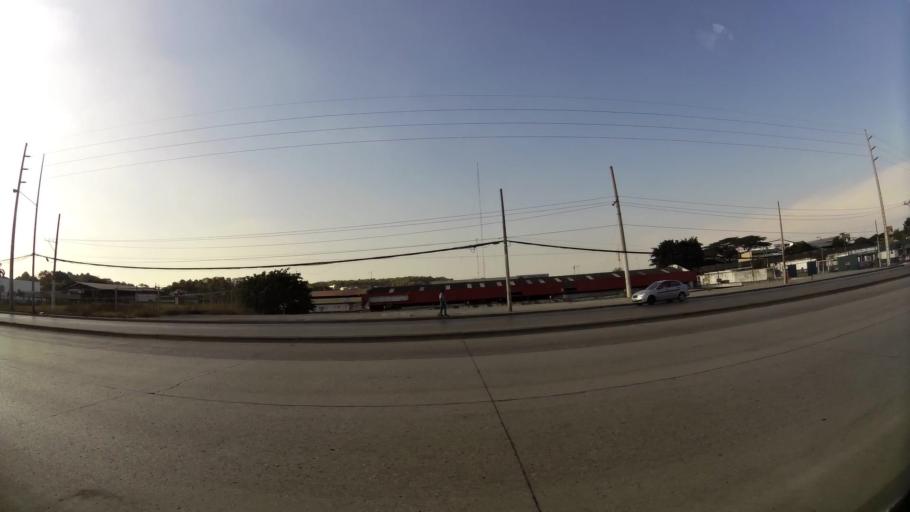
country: EC
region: Guayas
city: Guayaquil
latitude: -2.1436
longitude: -79.9196
